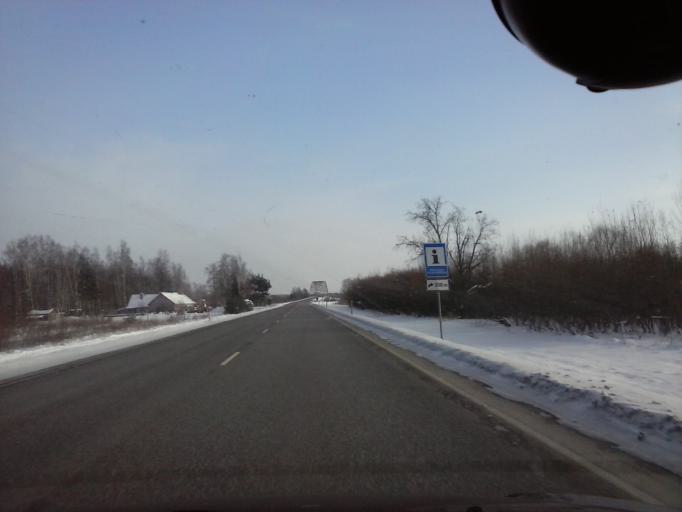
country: EE
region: Tartu
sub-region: Puhja vald
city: Puhja
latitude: 58.3905
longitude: 26.1278
